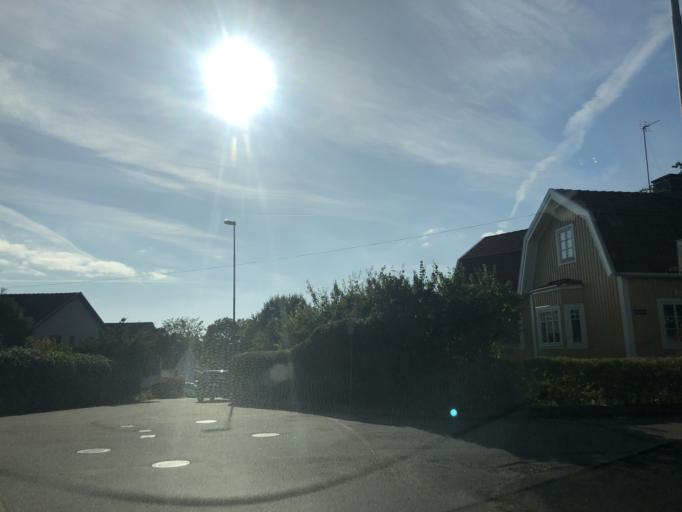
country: SE
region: Vaestra Goetaland
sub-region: Molndal
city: Moelndal
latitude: 57.6654
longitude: 12.0302
